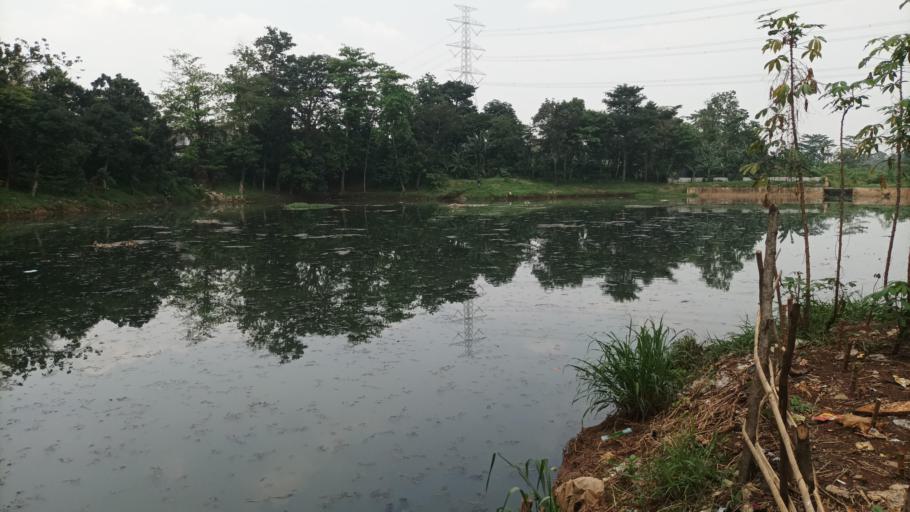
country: ID
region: West Java
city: Depok
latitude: -6.4226
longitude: 106.8496
